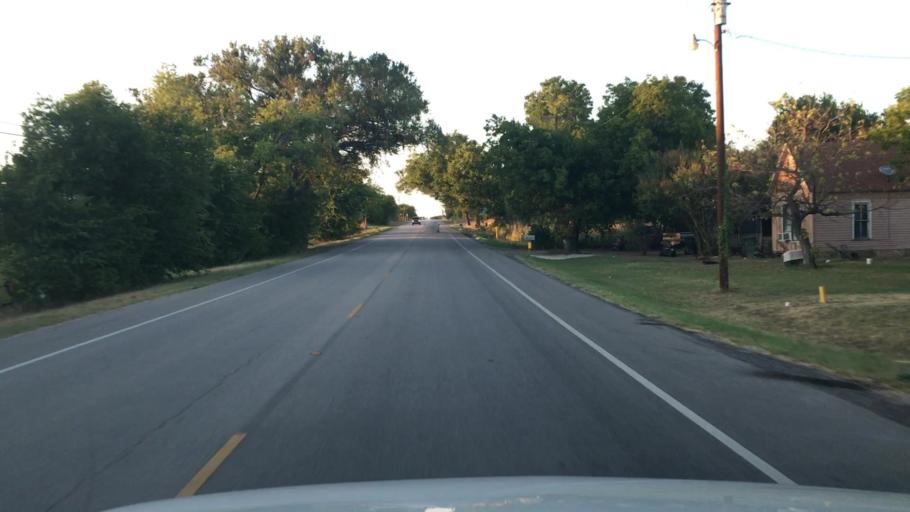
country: US
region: Texas
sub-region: Hamilton County
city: Hico
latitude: 31.9868
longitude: -98.0273
